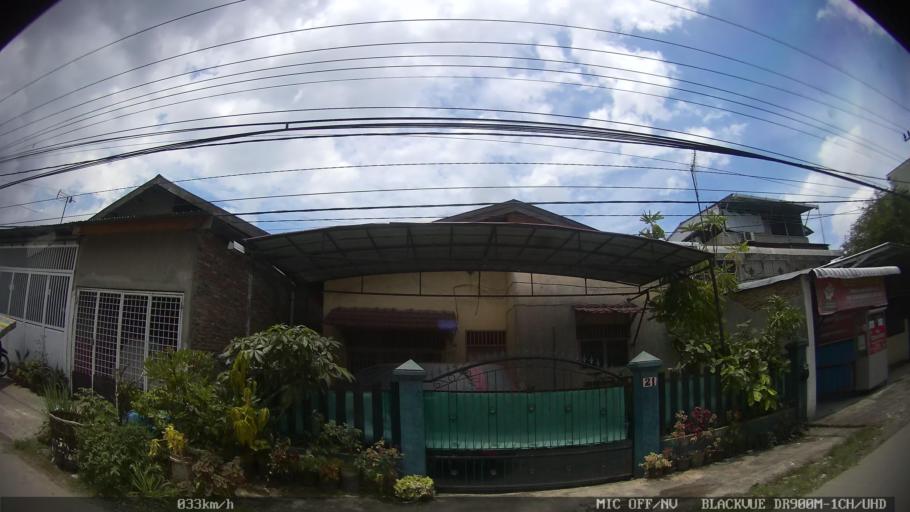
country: ID
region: North Sumatra
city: Medan
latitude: 3.6260
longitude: 98.6750
